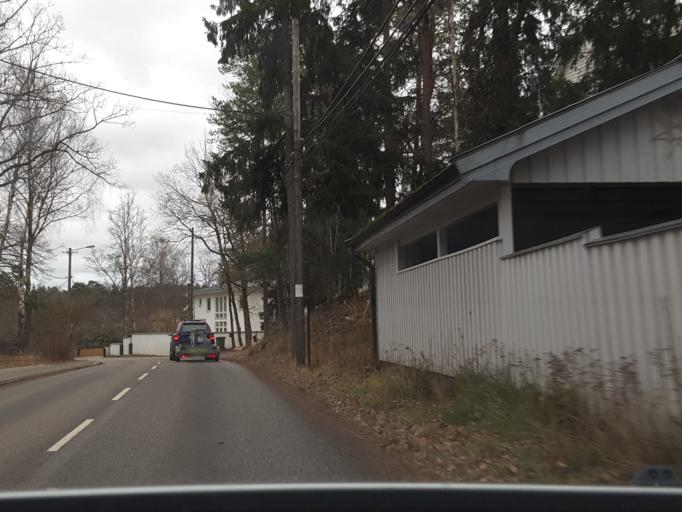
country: SE
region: Stockholm
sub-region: Nacka Kommun
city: Boo
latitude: 59.3261
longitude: 18.2869
